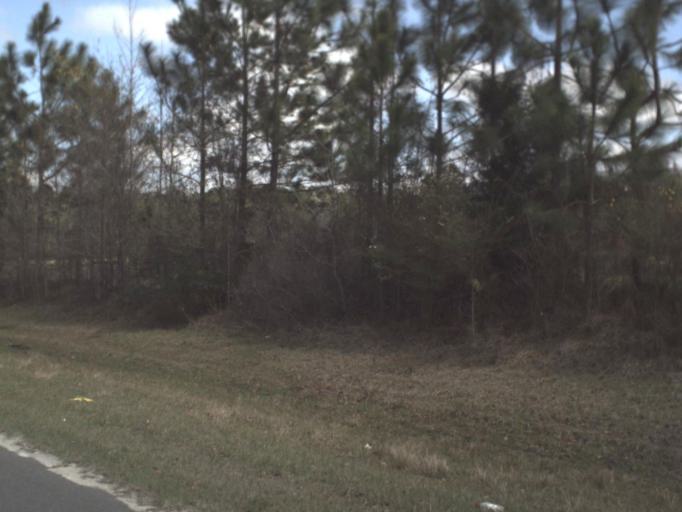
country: US
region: Florida
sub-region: Wakulla County
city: Crawfordville
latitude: 30.2755
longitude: -84.3575
